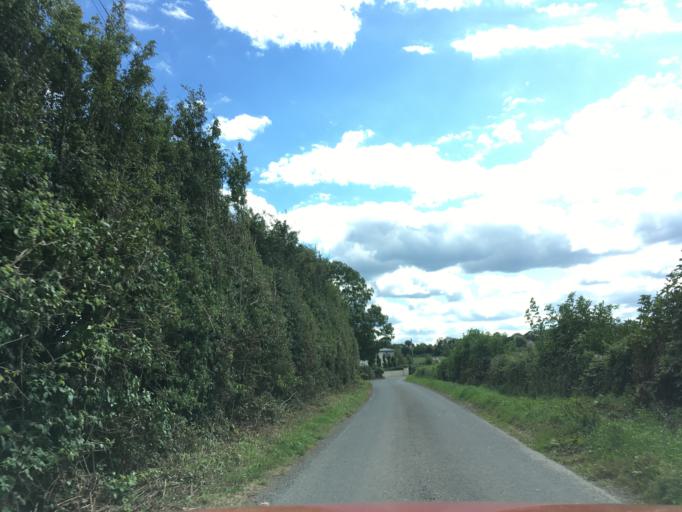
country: IE
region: Munster
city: Cashel
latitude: 52.4880
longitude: -7.9568
